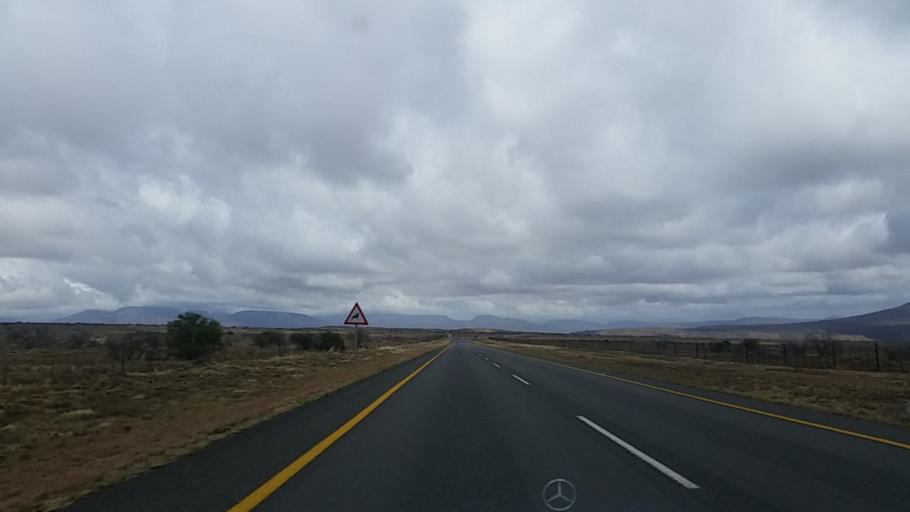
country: ZA
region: Eastern Cape
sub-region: Cacadu District Municipality
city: Graaff-Reinet
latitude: -32.1270
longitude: 24.5936
